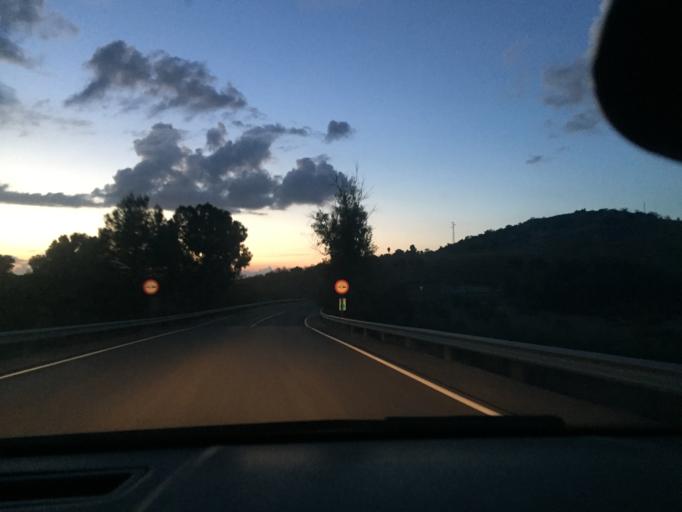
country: ES
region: Andalusia
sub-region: Provincia de Jaen
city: Mancha Real
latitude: 37.8004
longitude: -3.6593
